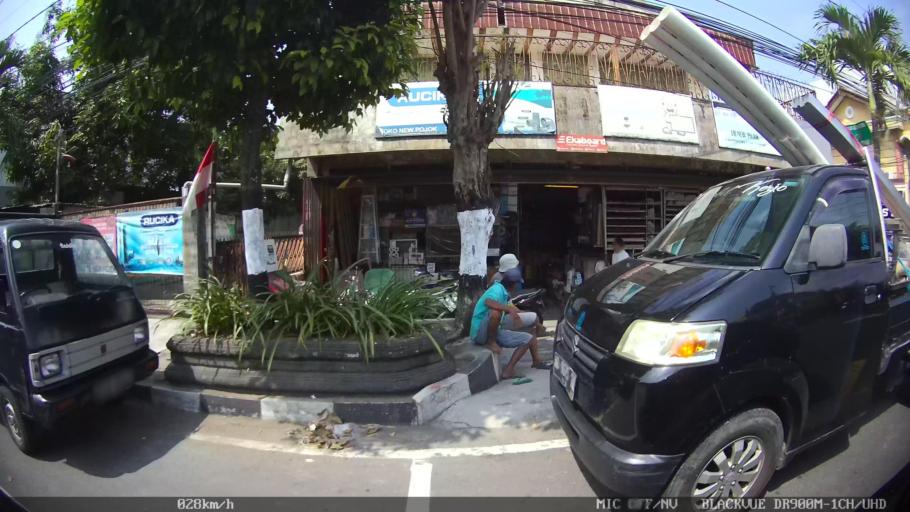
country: ID
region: Daerah Istimewa Yogyakarta
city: Yogyakarta
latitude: -7.8022
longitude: 110.3909
